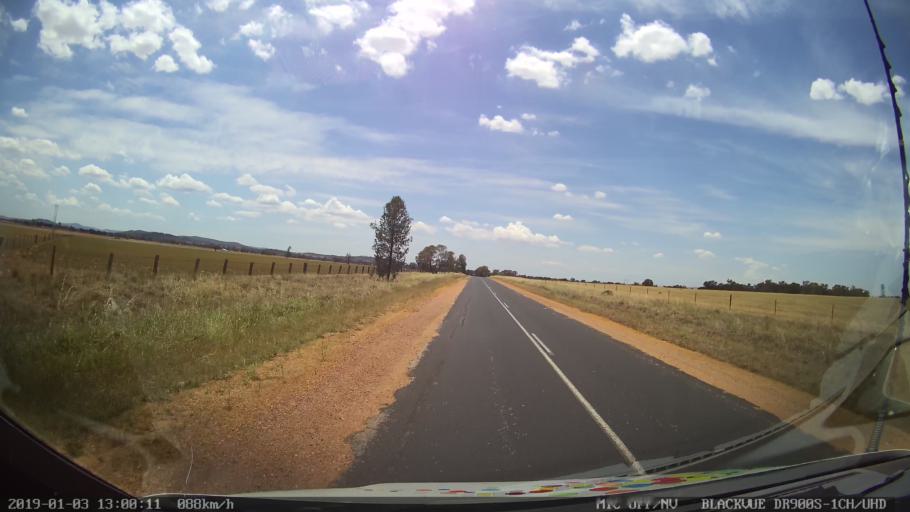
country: AU
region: New South Wales
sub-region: Cabonne
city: Canowindra
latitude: -33.6323
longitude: 148.3998
